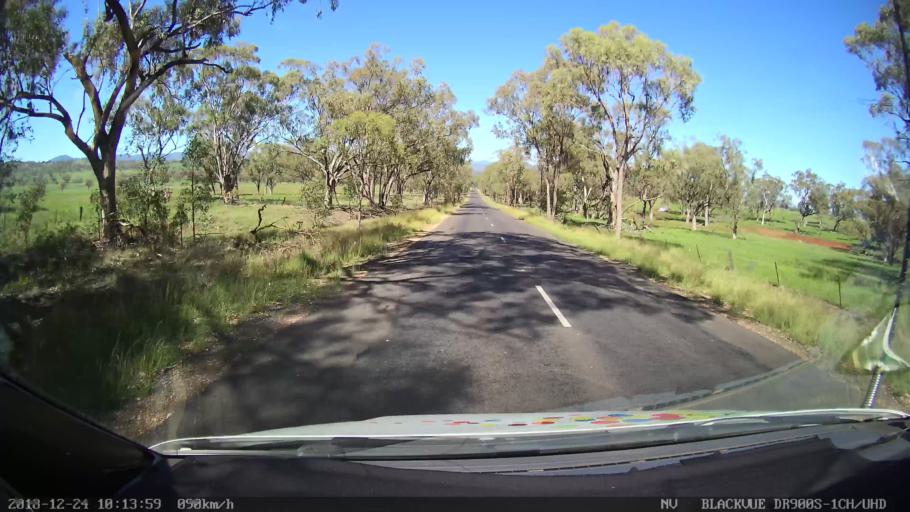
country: AU
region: New South Wales
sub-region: Liverpool Plains
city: Quirindi
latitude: -31.6943
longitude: 150.6344
